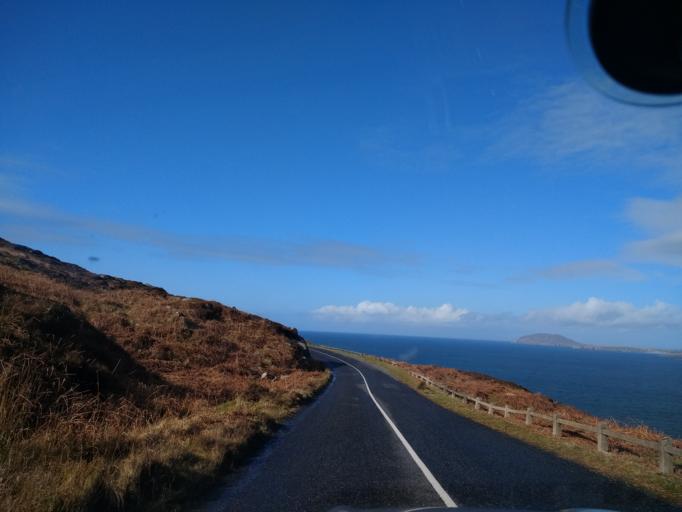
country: IE
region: Ulster
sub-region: County Donegal
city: Buncrana
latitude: 55.1836
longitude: -7.5866
